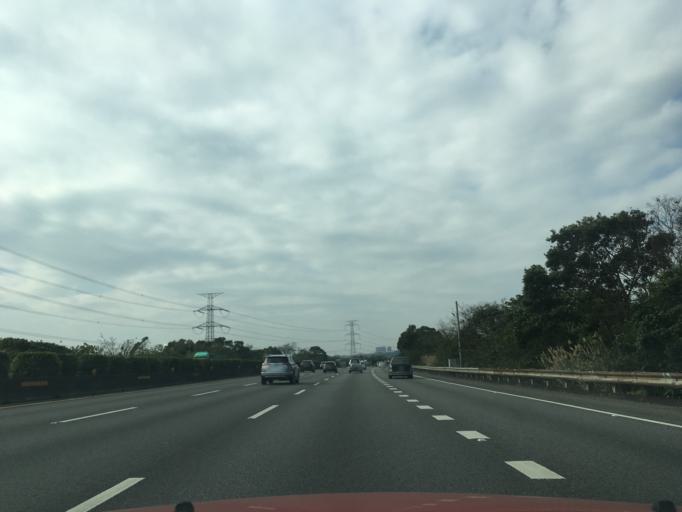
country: TW
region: Taiwan
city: Daxi
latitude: 24.9290
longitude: 121.3111
